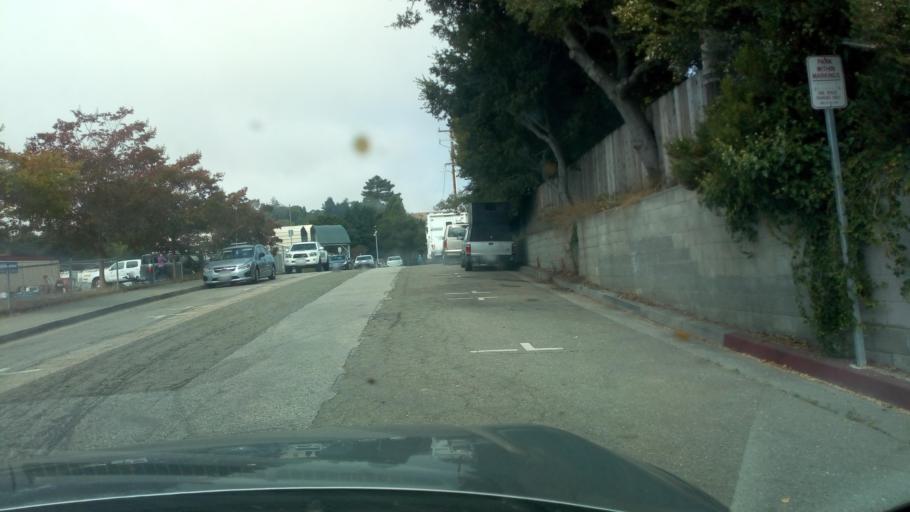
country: US
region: California
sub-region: Santa Cruz County
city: Santa Cruz
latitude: 36.9896
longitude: -122.0312
